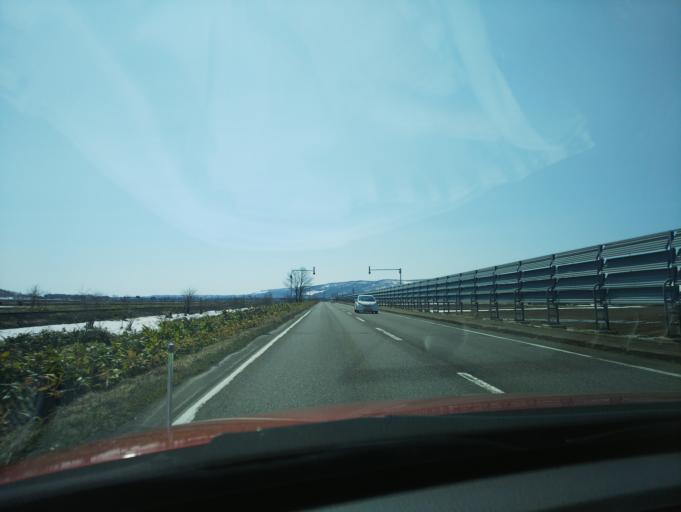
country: JP
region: Hokkaido
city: Nayoro
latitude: 44.2729
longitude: 142.3988
